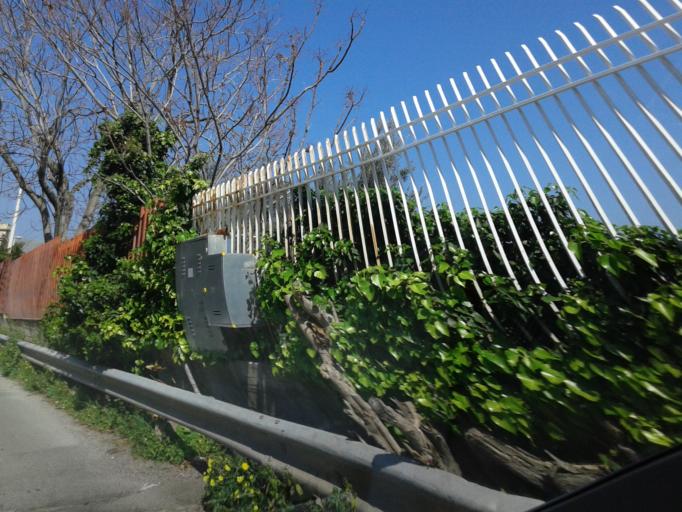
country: IT
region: Sicily
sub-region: Palermo
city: Piano dei Geli
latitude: 38.1107
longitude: 13.2991
